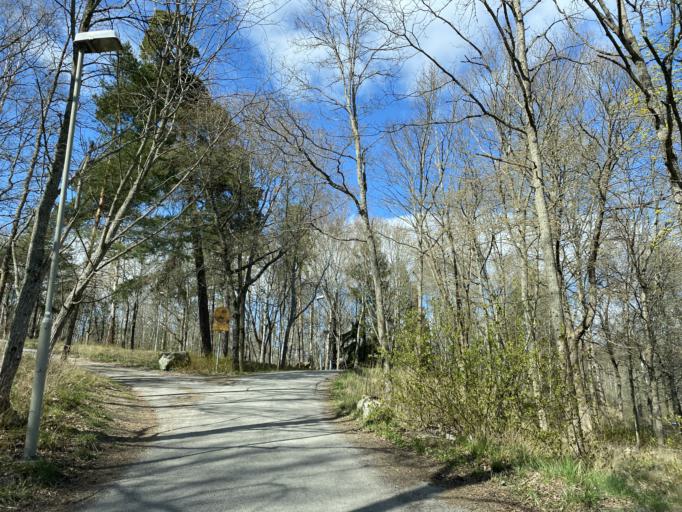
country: SE
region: Stockholm
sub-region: Nacka Kommun
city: Nacka
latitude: 59.3285
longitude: 18.1495
